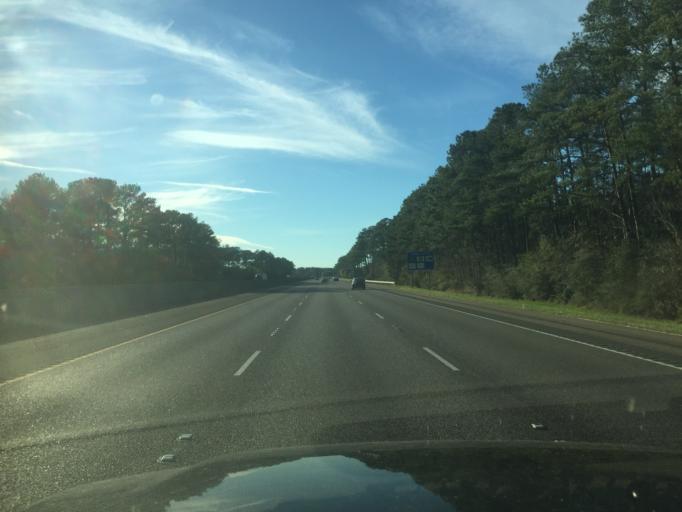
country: US
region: Louisiana
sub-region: Saint Tammany Parish
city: Slidell
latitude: 30.3102
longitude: -89.8015
